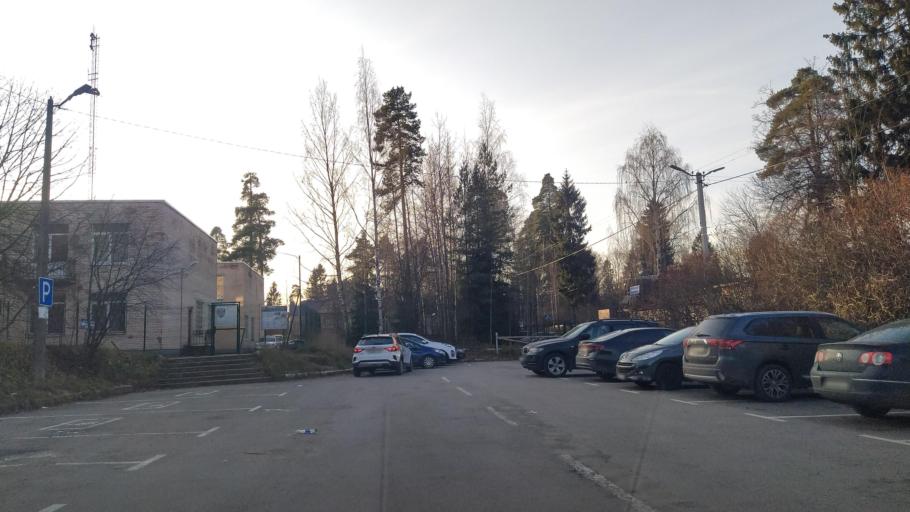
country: RU
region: Leningrad
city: Vsevolozhsk
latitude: 60.0244
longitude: 30.6815
